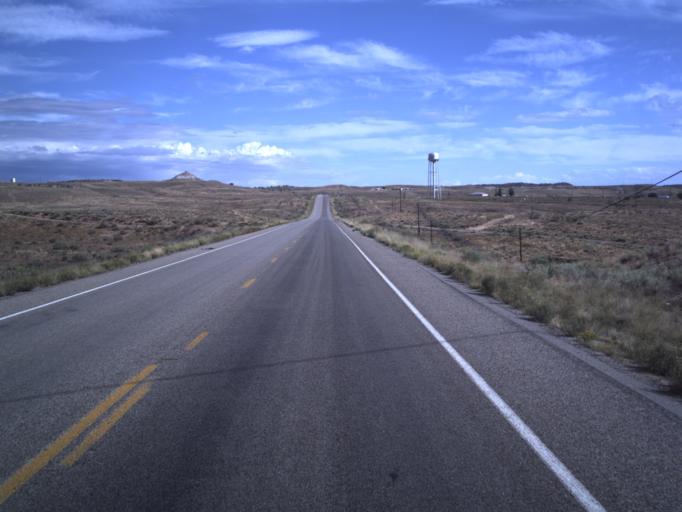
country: US
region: Colorado
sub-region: Montezuma County
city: Towaoc
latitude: 37.2042
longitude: -109.1601
